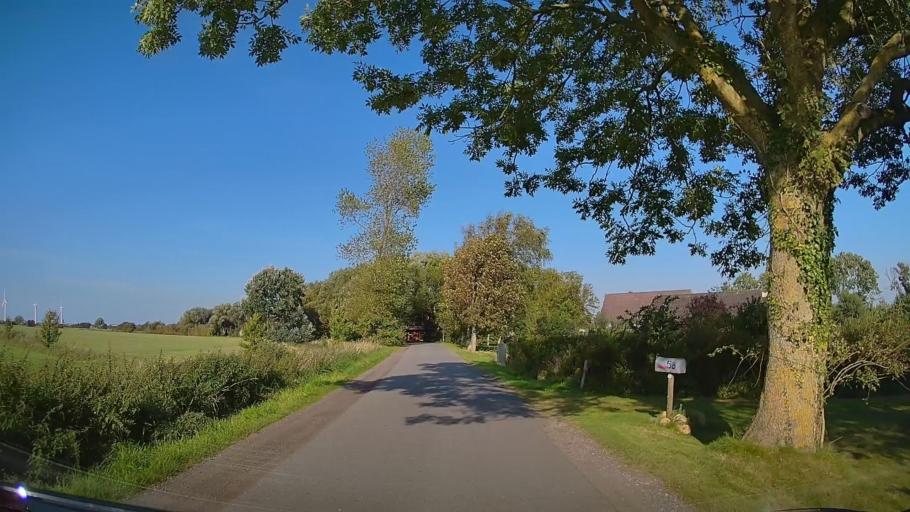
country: DE
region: Lower Saxony
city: Padingbuttel
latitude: 53.7150
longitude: 8.5168
